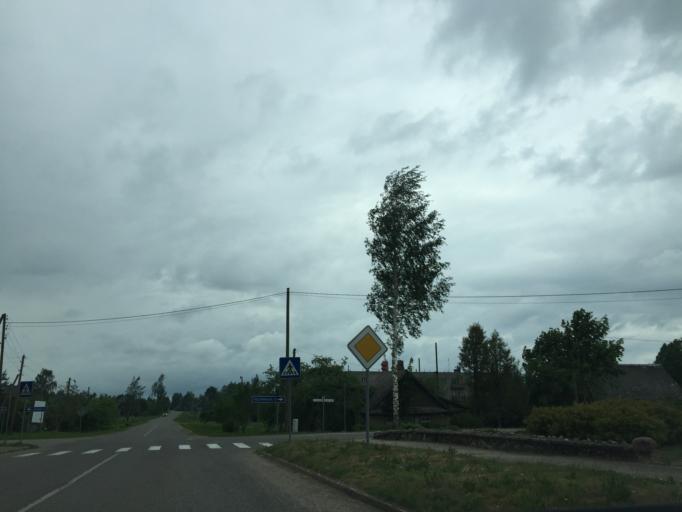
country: LV
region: Varkava
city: Vecvarkava
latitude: 56.0973
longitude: 26.5440
